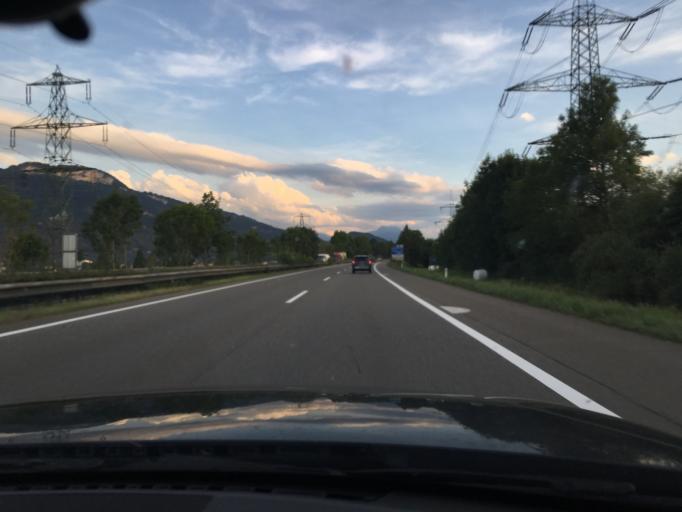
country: AT
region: Vorarlberg
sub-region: Politischer Bezirk Dornbirn
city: Hohenems
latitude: 47.3828
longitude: 9.6765
